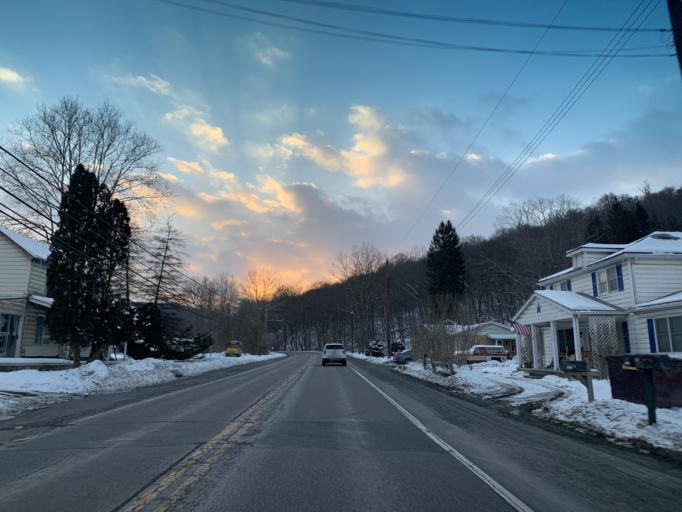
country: US
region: Maryland
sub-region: Allegany County
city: La Vale
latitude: 39.7003
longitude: -78.8491
